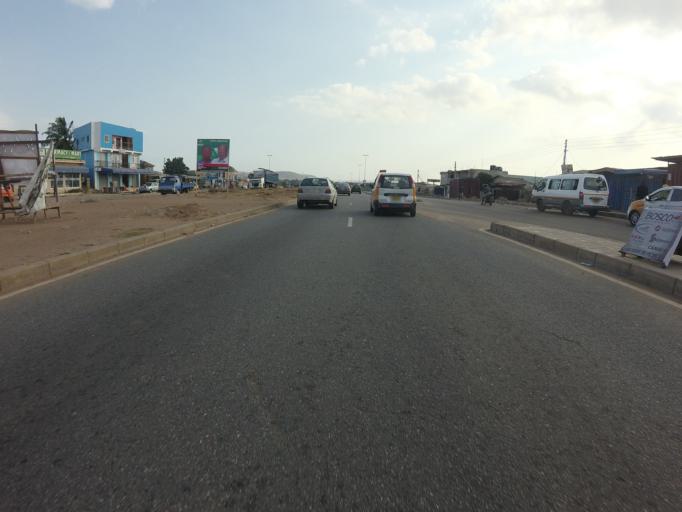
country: GH
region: Greater Accra
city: Achiaman
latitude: 5.6456
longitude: -0.3102
